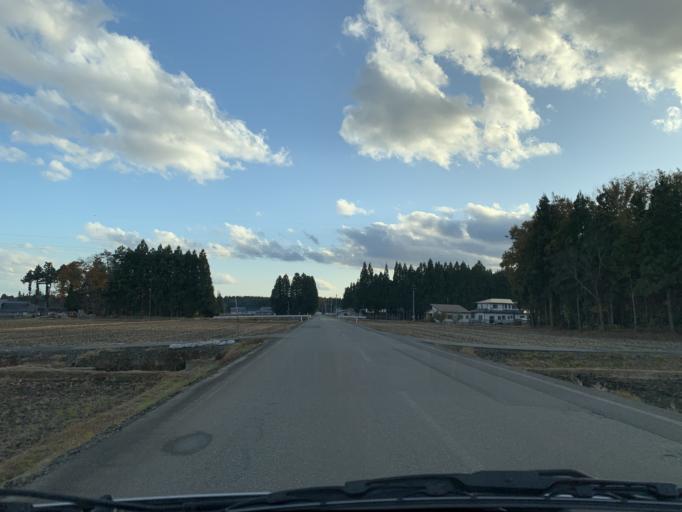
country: JP
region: Iwate
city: Mizusawa
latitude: 39.1277
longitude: 141.0368
